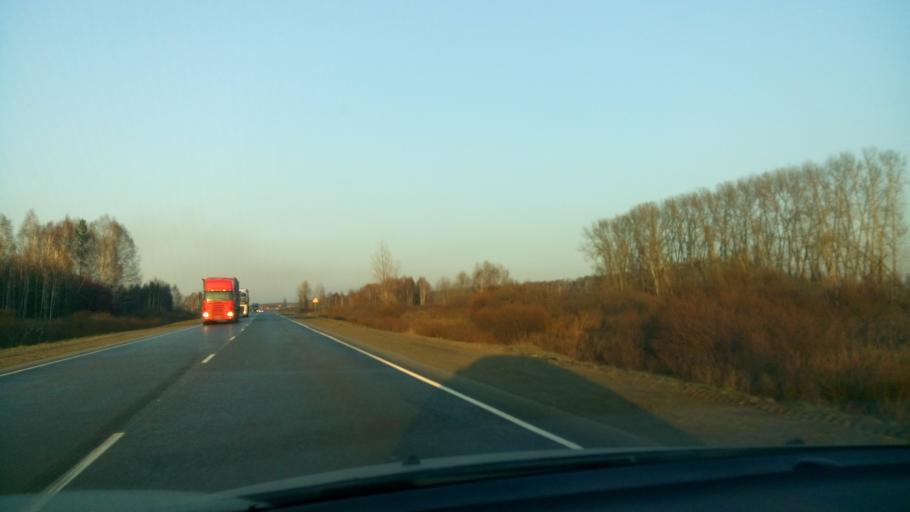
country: RU
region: Sverdlovsk
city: Obukhovskoye
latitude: 56.8326
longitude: 62.5686
